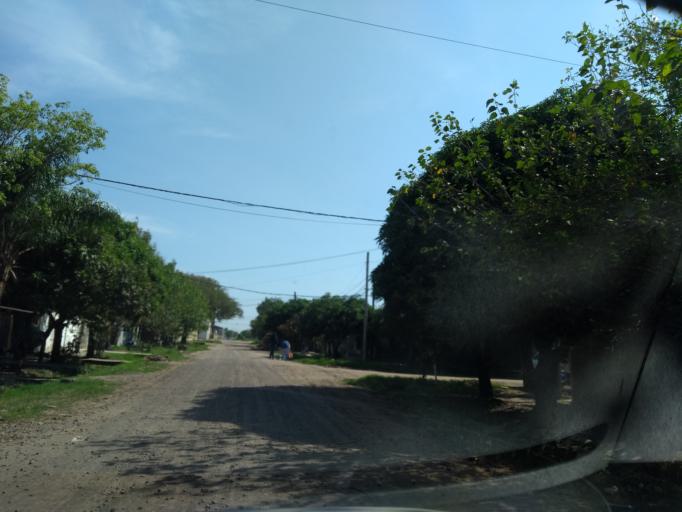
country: AR
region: Chaco
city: Barranqueras
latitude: -27.4779
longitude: -58.9616
